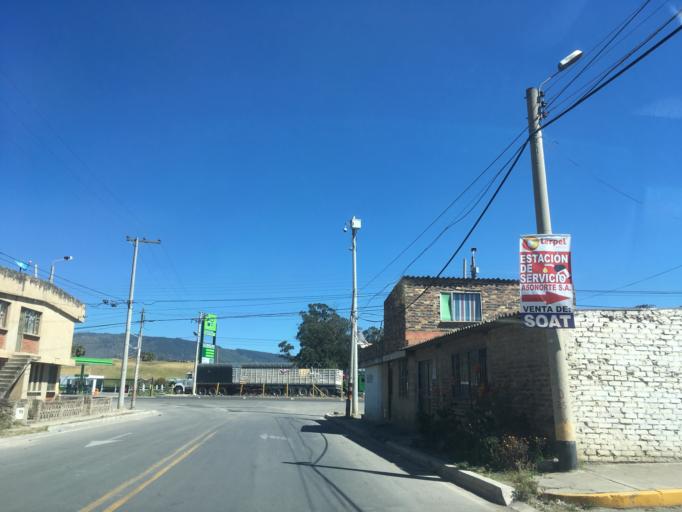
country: CO
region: Boyaca
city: Sogamoso
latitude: 5.7238
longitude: -72.9432
